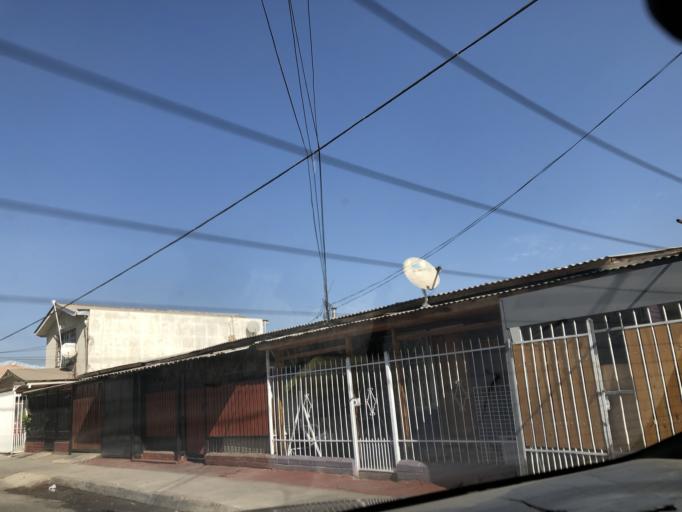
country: CL
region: Santiago Metropolitan
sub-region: Provincia de Santiago
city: La Pintana
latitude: -33.5872
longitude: -70.6034
